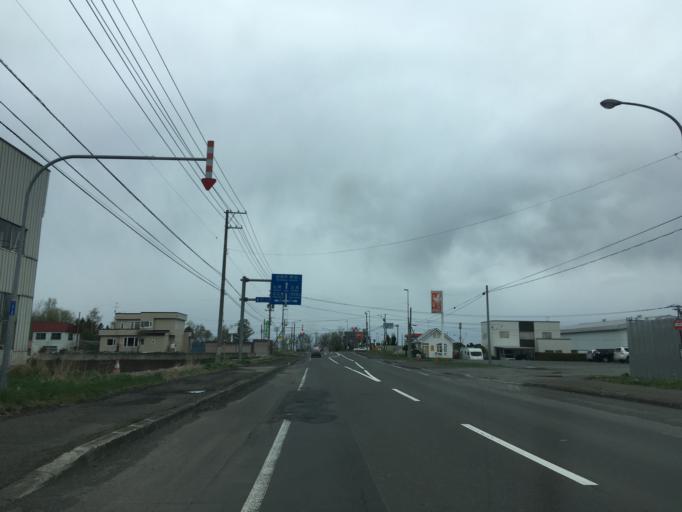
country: JP
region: Hokkaido
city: Chitose
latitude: 42.9490
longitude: 141.8028
